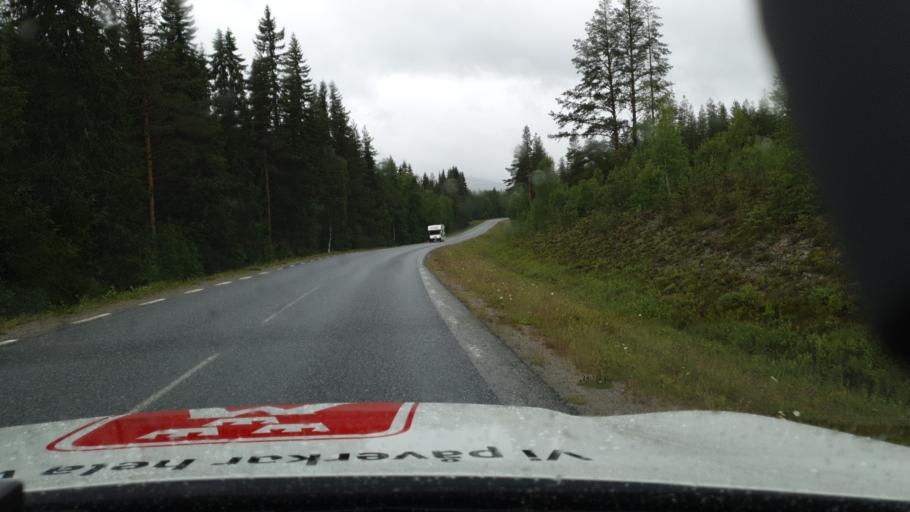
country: SE
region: Vaesterbotten
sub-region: Asele Kommun
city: Asele
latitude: 64.2075
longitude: 17.3228
